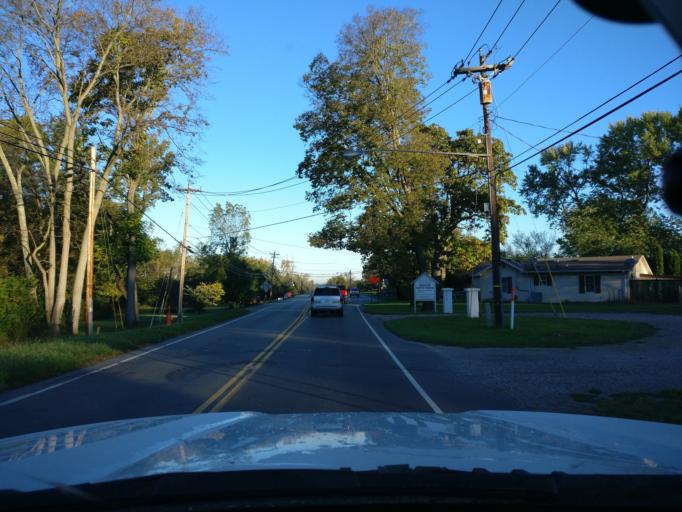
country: US
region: Ohio
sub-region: Warren County
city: Franklin
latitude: 39.5298
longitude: -84.2823
